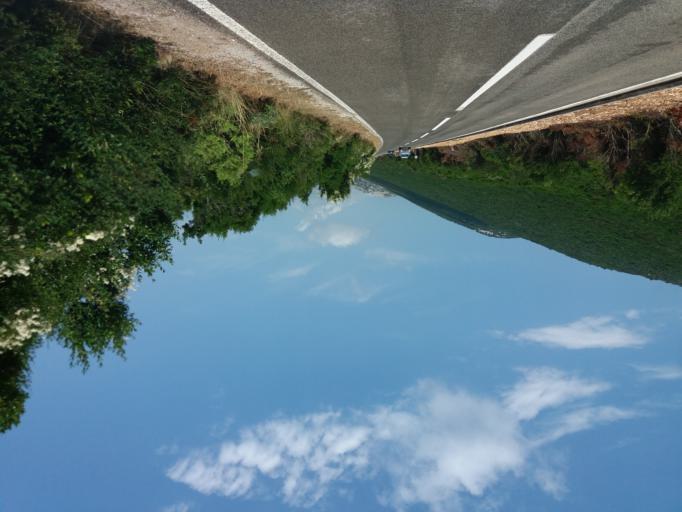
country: HR
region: Zadarska
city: Sali
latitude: 43.9928
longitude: 15.0646
